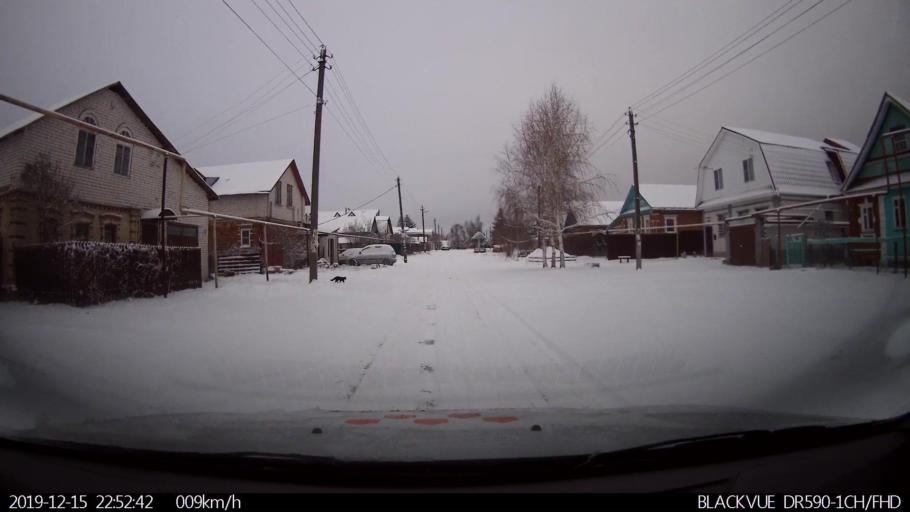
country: RU
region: Nizjnij Novgorod
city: Afonino
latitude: 56.2192
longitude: 44.1139
